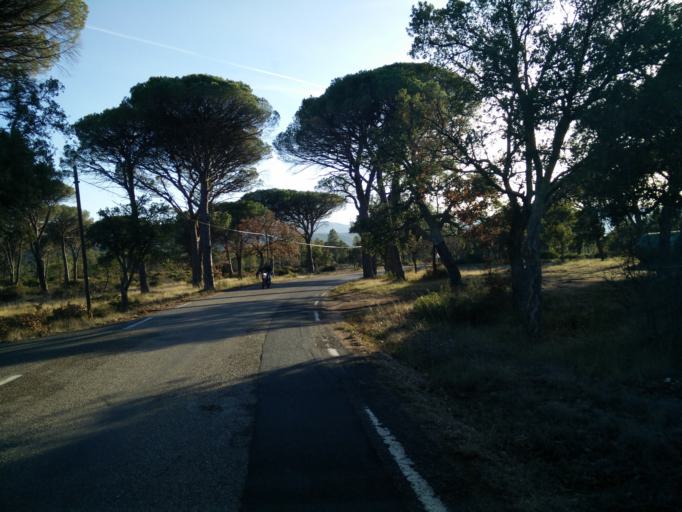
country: FR
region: Provence-Alpes-Cote d'Azur
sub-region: Departement du Var
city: La Garde-Freinet
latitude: 43.3646
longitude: 6.4460
